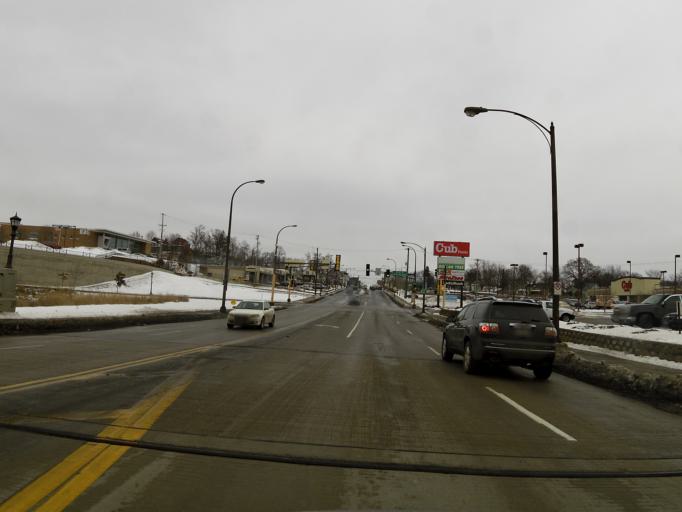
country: US
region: Minnesota
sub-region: Ramsey County
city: Saint Paul
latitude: 44.9664
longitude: -93.0660
